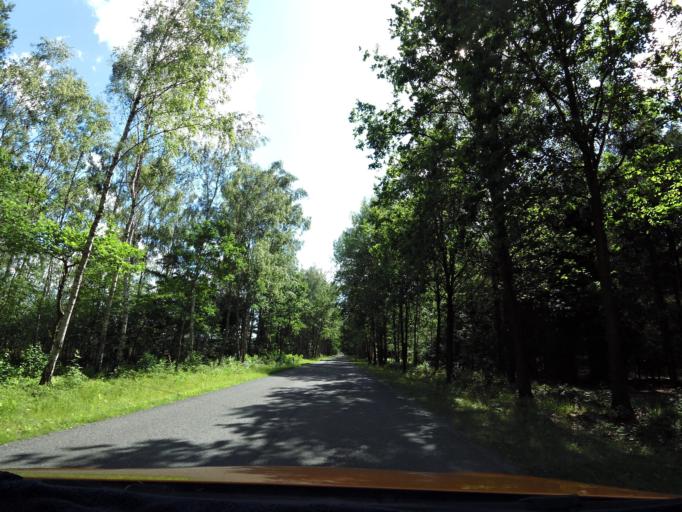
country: DE
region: Brandenburg
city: Erkner
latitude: 52.3186
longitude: 13.7544
